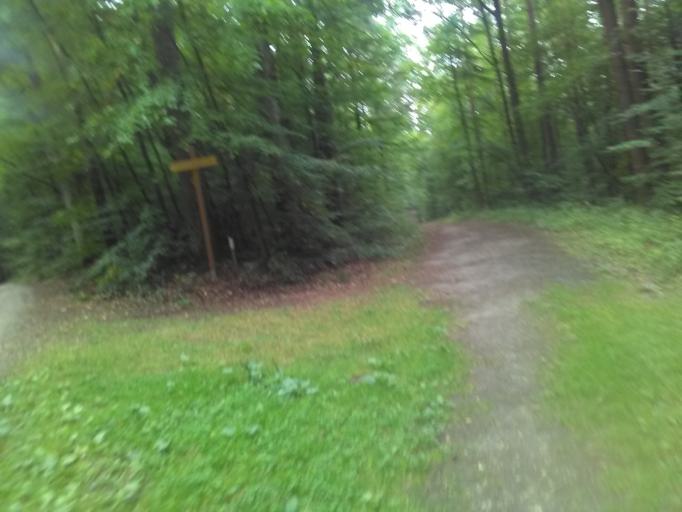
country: DE
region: Bavaria
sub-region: Upper Franconia
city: Bamberg
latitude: 49.8633
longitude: 10.8991
